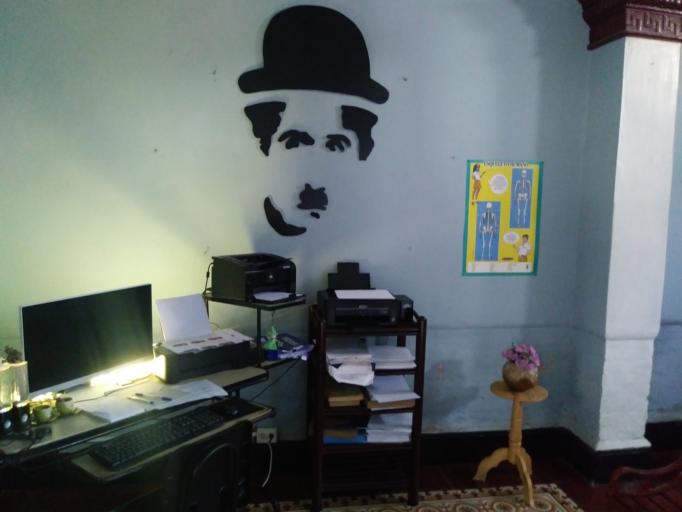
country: CU
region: Villa Clara
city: Sagua la Grande
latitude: 22.8075
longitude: -80.0732
